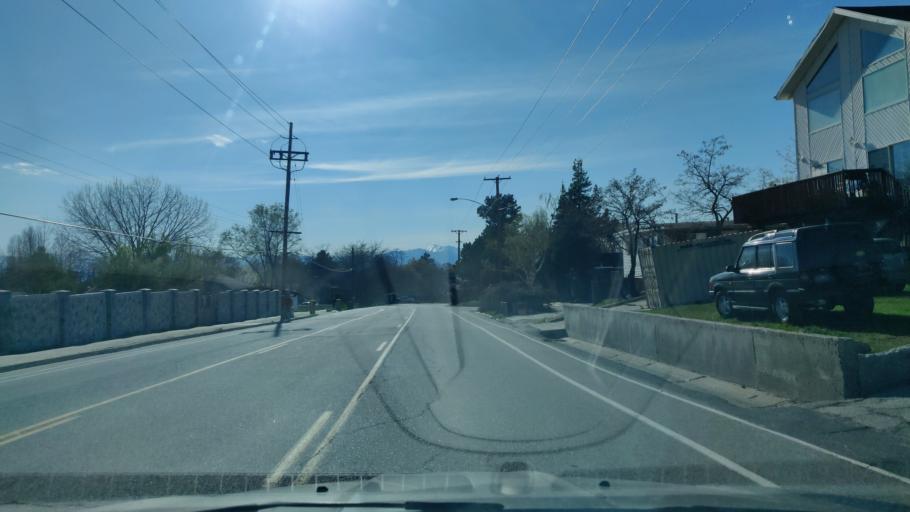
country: US
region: Utah
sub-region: Salt Lake County
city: Cottonwood Heights
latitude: 40.6094
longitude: -111.8137
